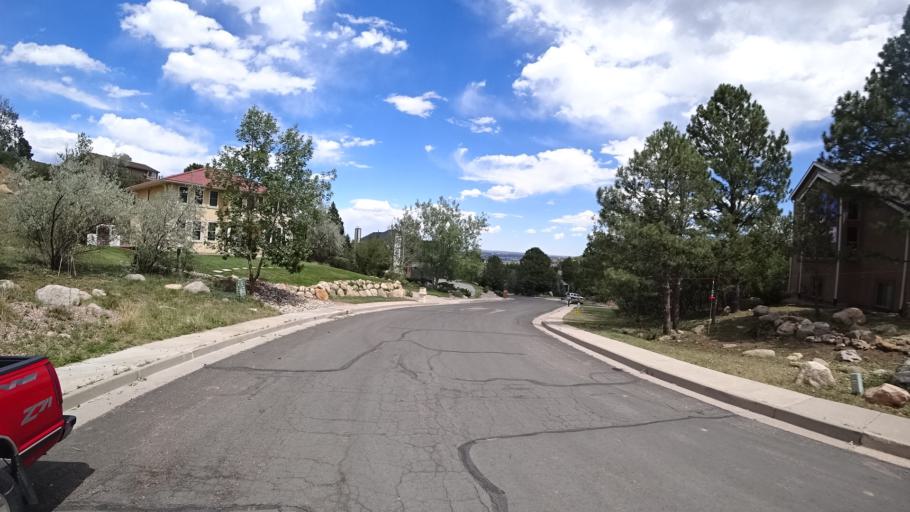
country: US
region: Colorado
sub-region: El Paso County
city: Stratmoor
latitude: 38.7708
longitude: -104.8346
